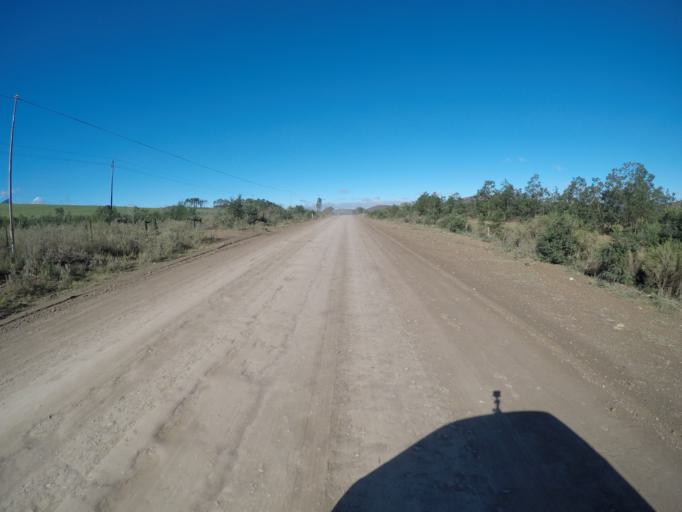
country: ZA
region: Western Cape
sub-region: Overberg District Municipality
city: Caledon
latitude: -34.0657
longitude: 19.6284
